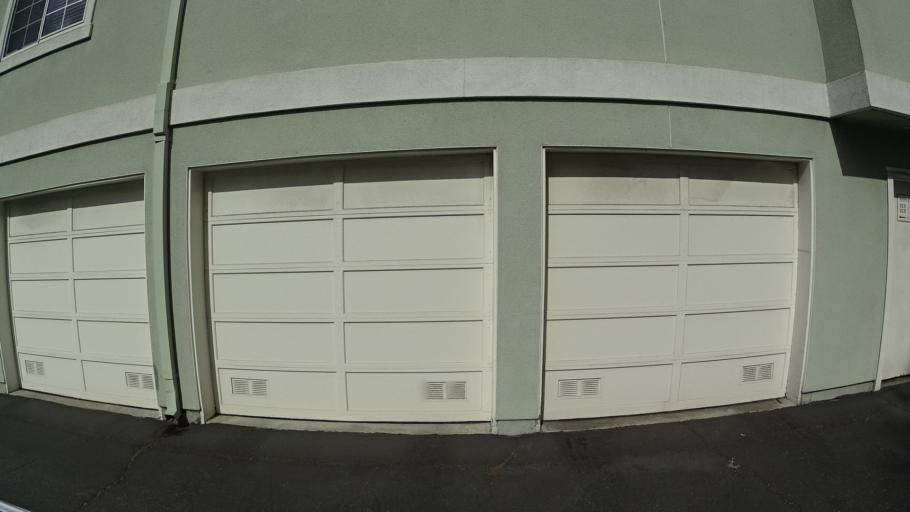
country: US
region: California
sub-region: San Mateo County
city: Daly City
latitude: 37.7066
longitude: -122.4406
